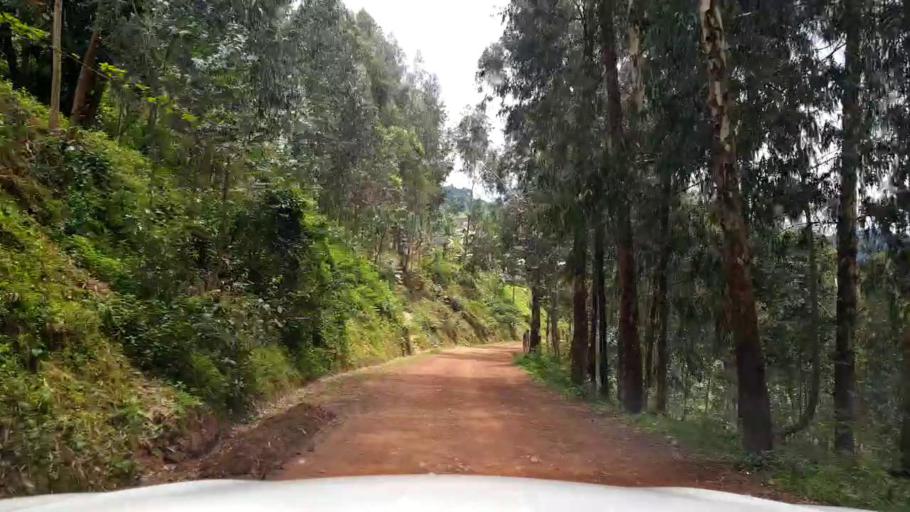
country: UG
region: Western Region
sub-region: Kabale District
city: Kabale
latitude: -1.4320
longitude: 29.8685
